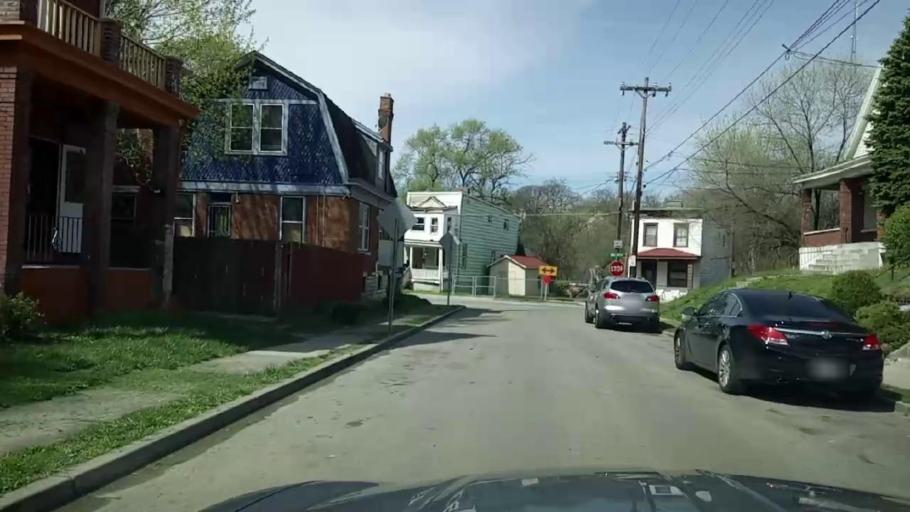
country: US
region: Kentucky
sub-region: Campbell County
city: Newport
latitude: 39.1223
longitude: -84.5126
